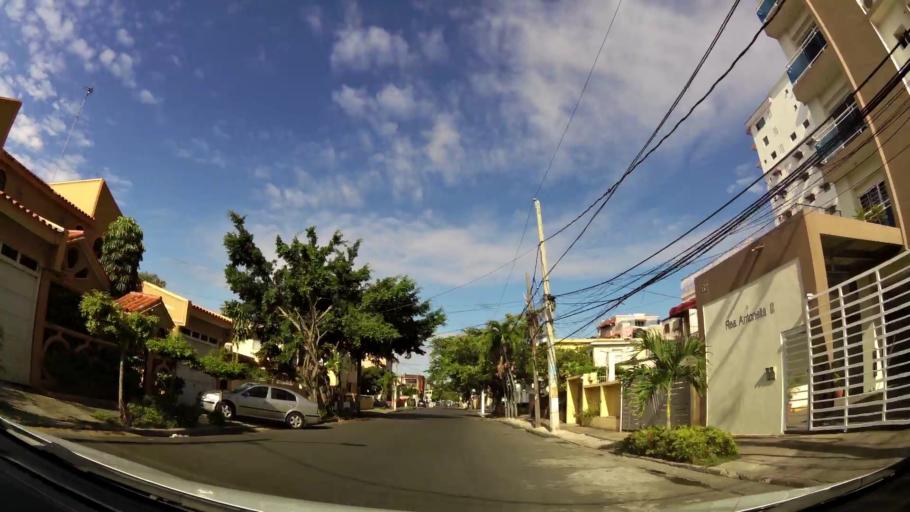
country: DO
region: Santo Domingo
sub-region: Santo Domingo
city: Santo Domingo Este
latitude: 18.4873
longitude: -69.8683
